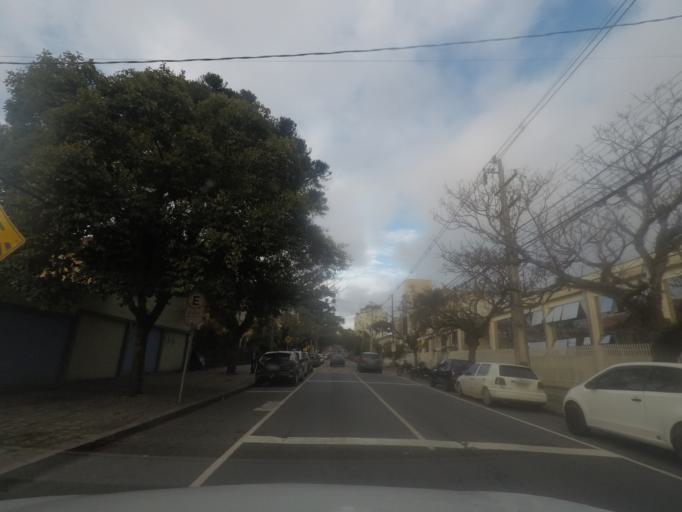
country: BR
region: Parana
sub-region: Curitiba
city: Curitiba
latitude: -25.4315
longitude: -49.2460
